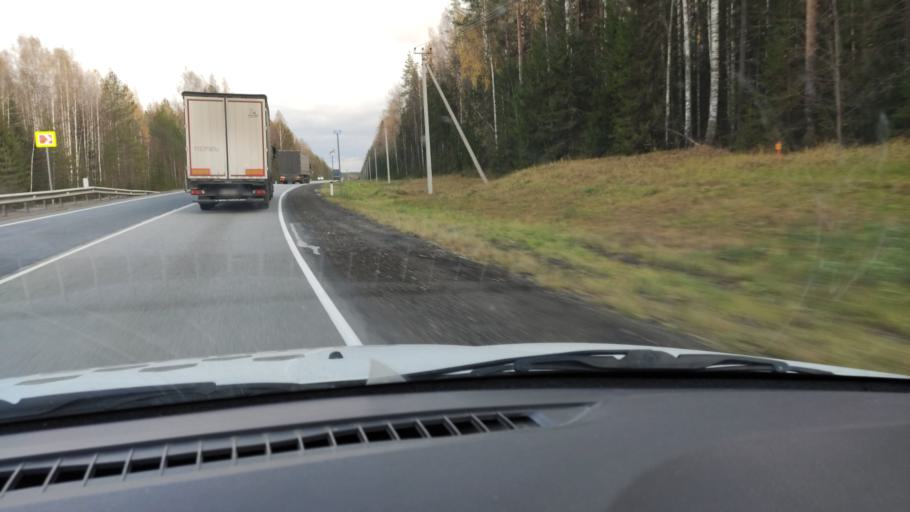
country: RU
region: Kirov
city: Dubrovka
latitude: 58.9125
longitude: 51.1685
